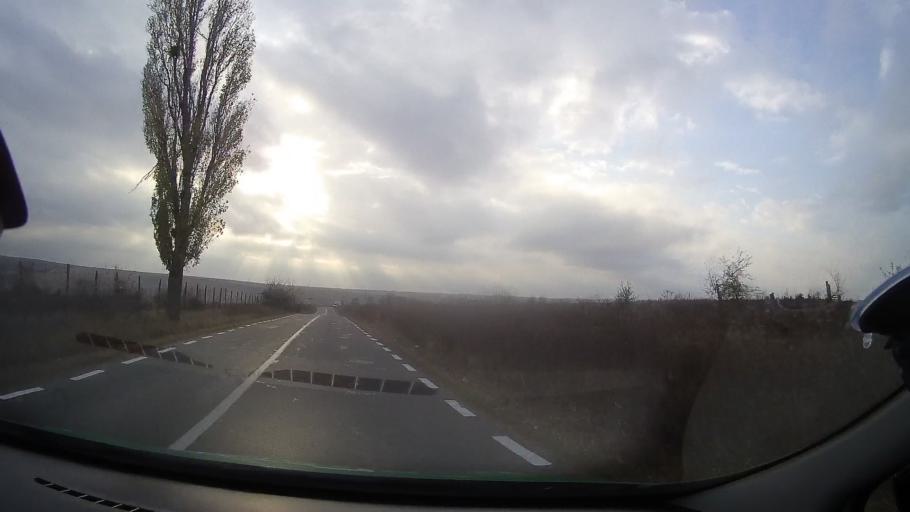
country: RO
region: Constanta
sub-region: Municipiul Medgidia
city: Medgidia
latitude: 44.2395
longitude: 28.2513
